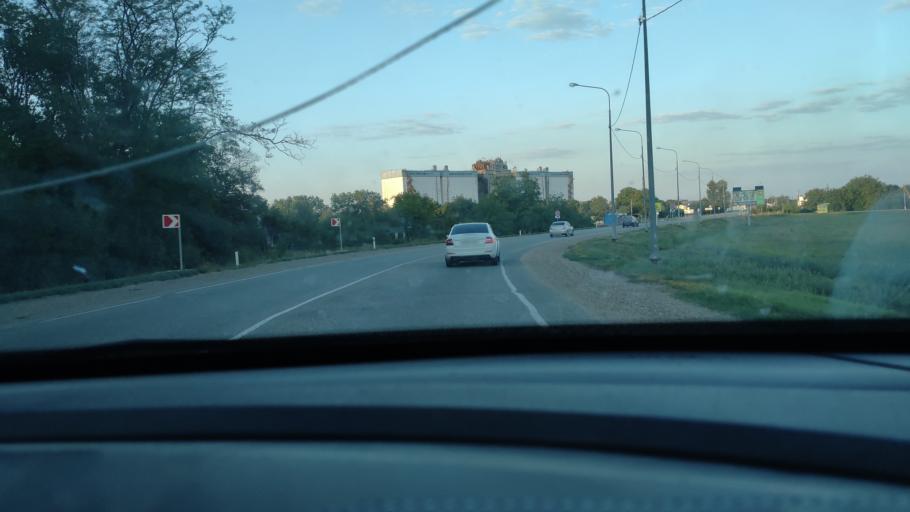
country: RU
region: Krasnodarskiy
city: Novominskaya
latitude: 46.3237
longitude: 38.9353
